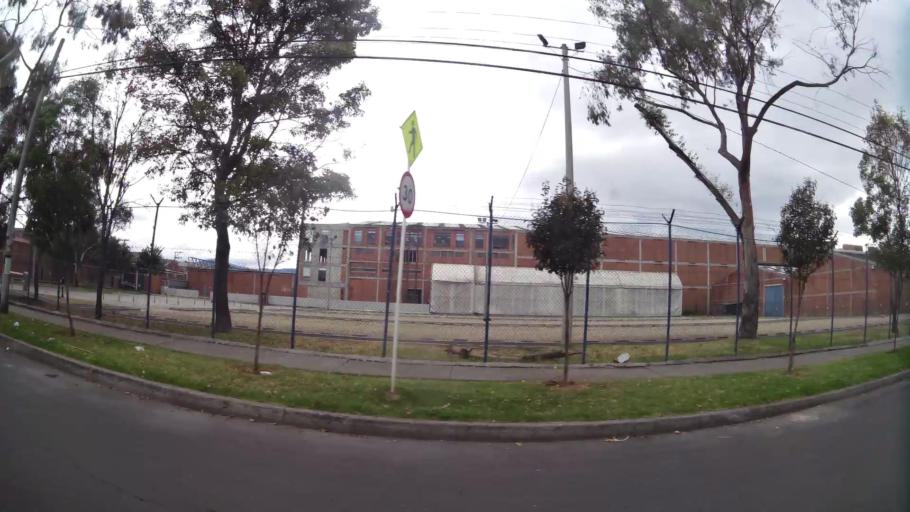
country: CO
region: Bogota D.C.
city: Bogota
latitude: 4.6010
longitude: -74.1390
